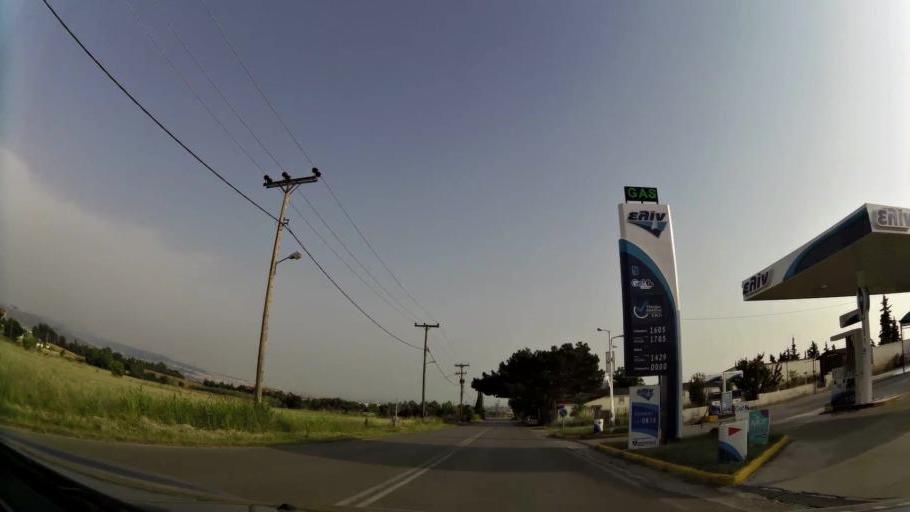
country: GR
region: Central Macedonia
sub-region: Nomos Thessalonikis
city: Oraiokastro
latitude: 40.7164
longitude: 22.9104
